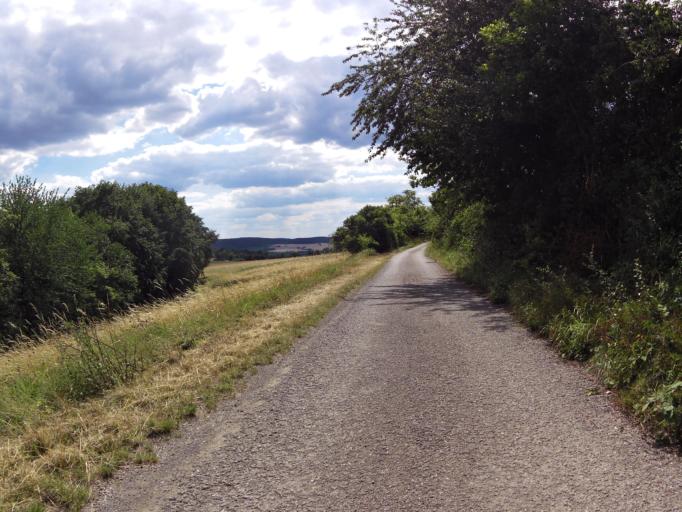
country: DE
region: Bavaria
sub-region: Regierungsbezirk Unterfranken
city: Retzstadt
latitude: 49.8910
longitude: 9.8715
